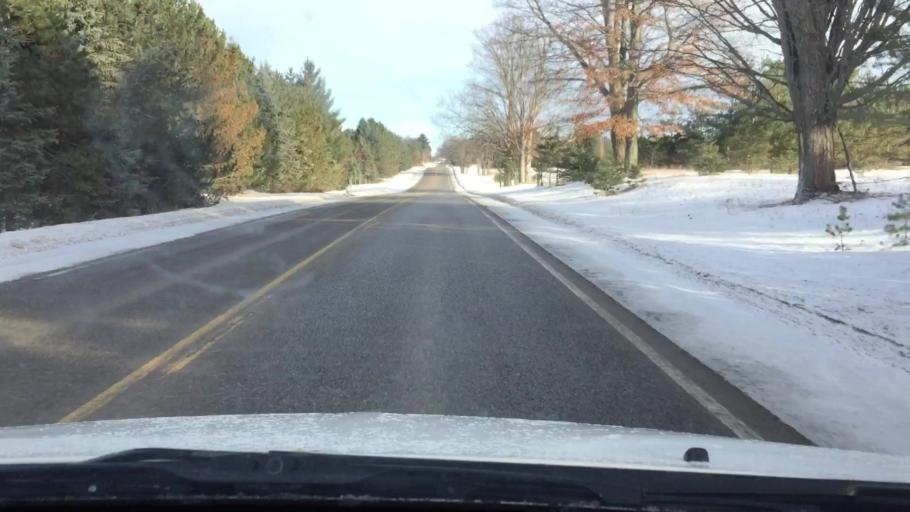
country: US
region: Michigan
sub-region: Kalkaska County
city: Kalkaska
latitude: 44.6408
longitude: -85.2408
